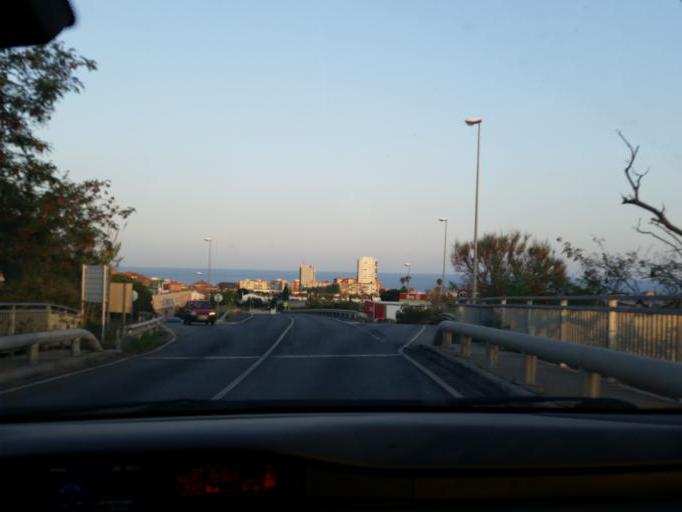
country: ES
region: Catalonia
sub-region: Provincia de Barcelona
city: Vilassar de Mar
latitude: 41.5130
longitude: 2.3801
